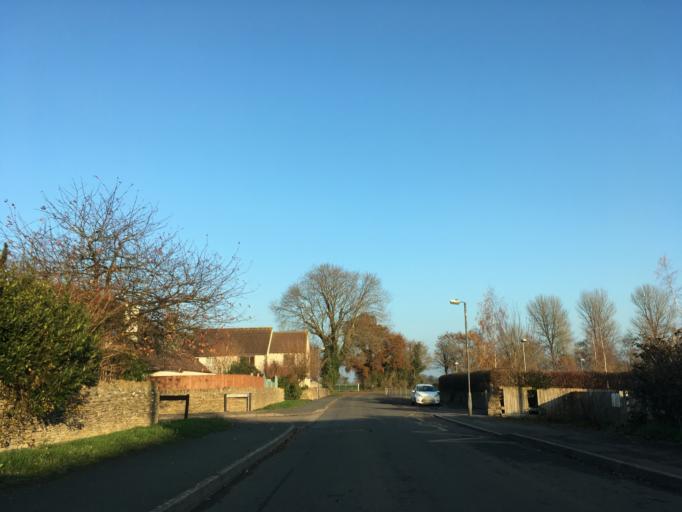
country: GB
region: England
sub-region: Wiltshire
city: Nettleton
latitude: 51.5263
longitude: -2.2742
